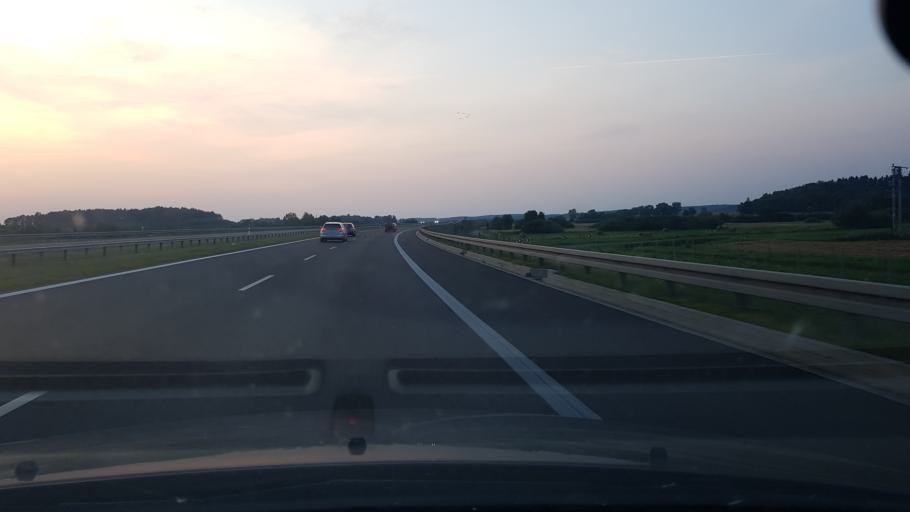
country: PL
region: Warmian-Masurian Voivodeship
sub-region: Powiat nidzicki
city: Nidzica
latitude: 53.3785
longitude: 20.3754
